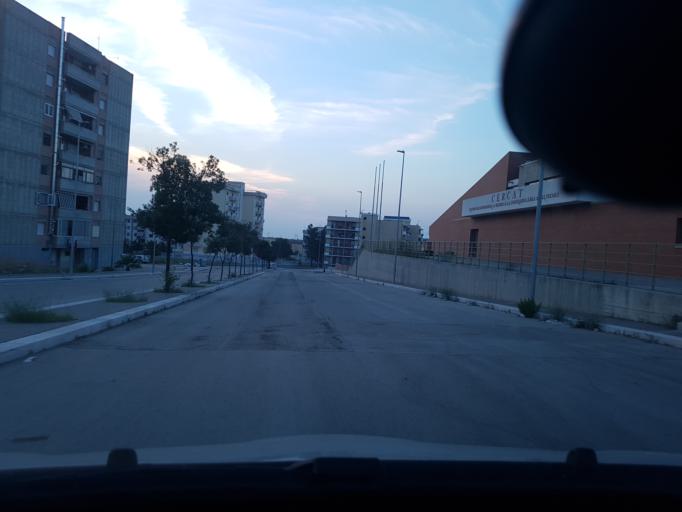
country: IT
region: Apulia
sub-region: Provincia di Foggia
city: Cerignola
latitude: 41.2589
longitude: 15.8769
